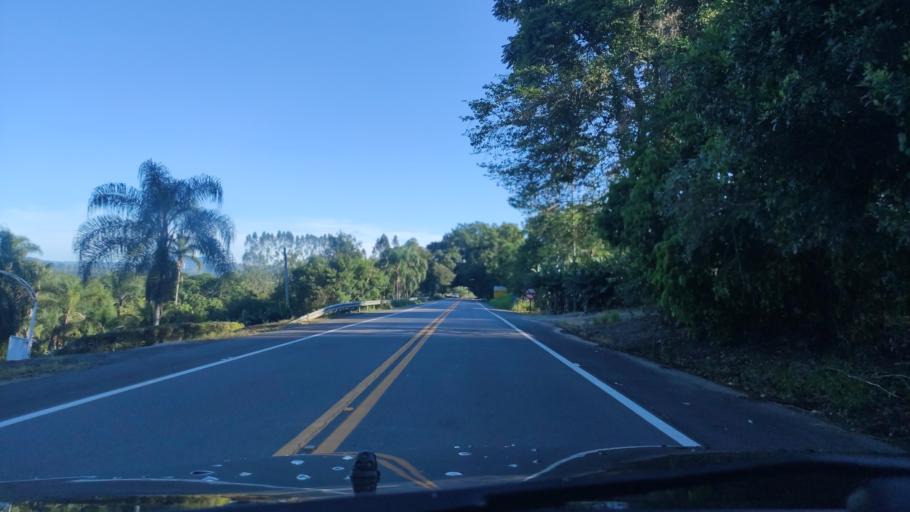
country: BR
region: Sao Paulo
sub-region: Socorro
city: Socorro
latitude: -22.5569
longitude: -46.5842
